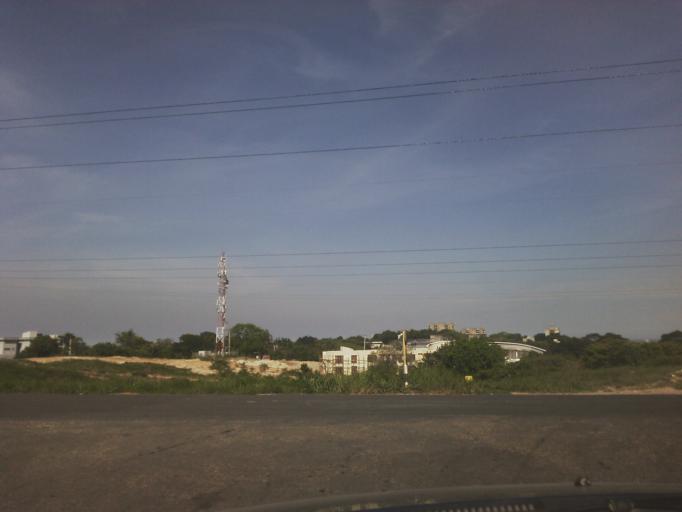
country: TZ
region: Dar es Salaam
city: Magomeni
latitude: -6.7785
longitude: 39.1989
